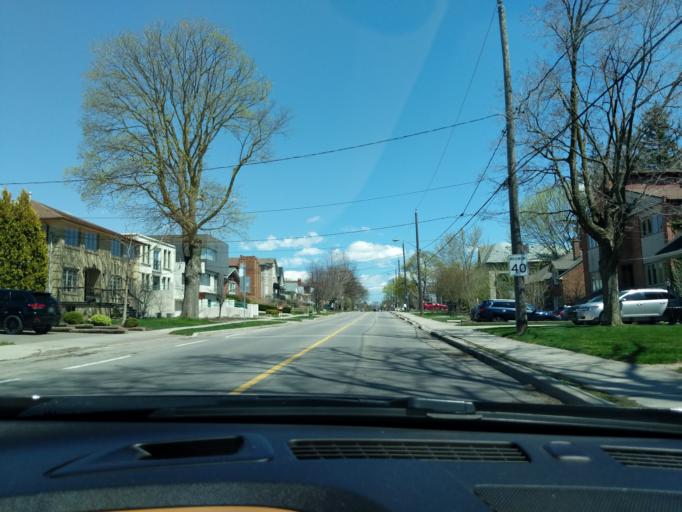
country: CA
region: Ontario
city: Toronto
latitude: 43.7114
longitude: -79.4327
